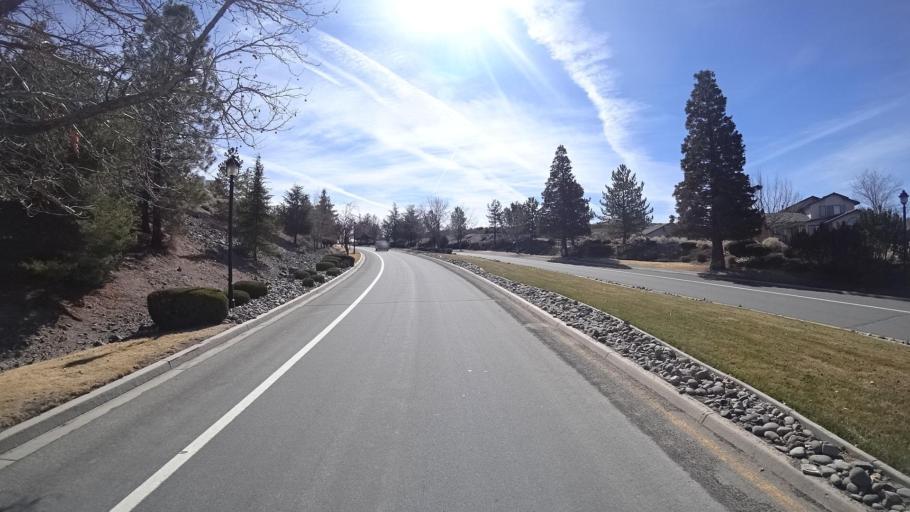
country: US
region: Nevada
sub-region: Washoe County
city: Sparks
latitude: 39.5802
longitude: -119.7024
